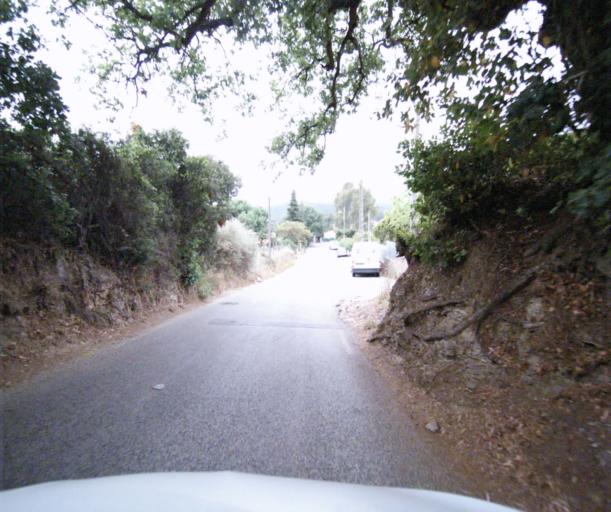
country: FR
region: Provence-Alpes-Cote d'Azur
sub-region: Departement du Var
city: Six-Fours-les-Plages
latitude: 43.0873
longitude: 5.8663
